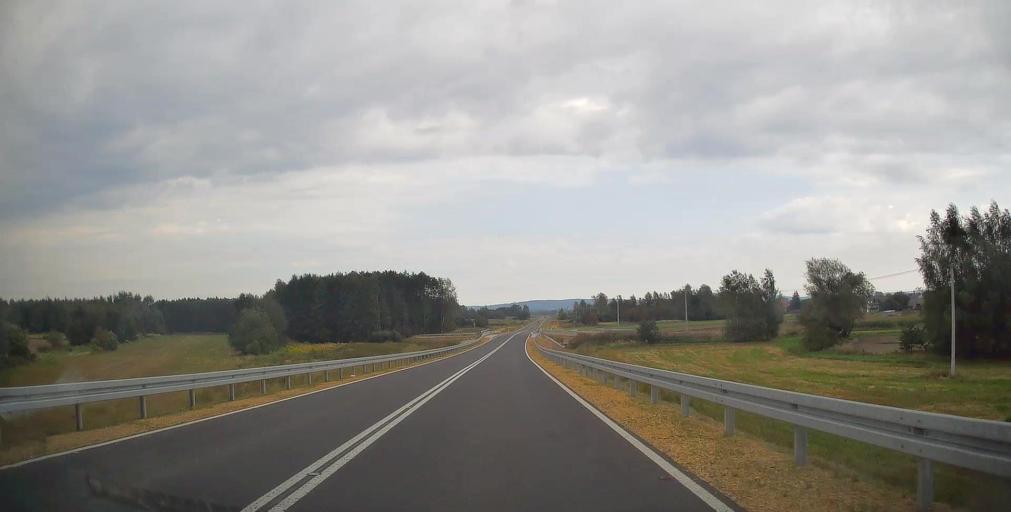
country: PL
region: Lesser Poland Voivodeship
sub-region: Powiat oswiecimski
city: Zator
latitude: 50.0048
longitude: 19.4231
